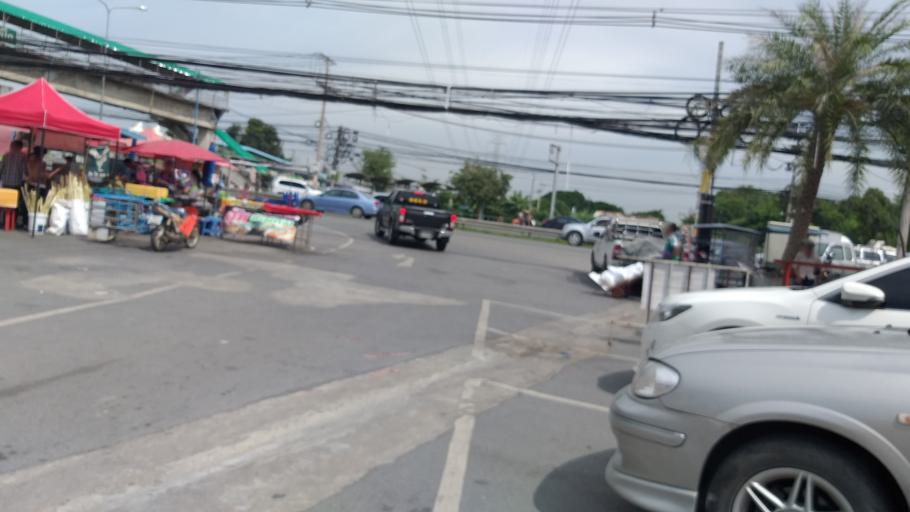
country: TH
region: Pathum Thani
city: Khlong Luang
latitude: 13.9959
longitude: 100.6664
